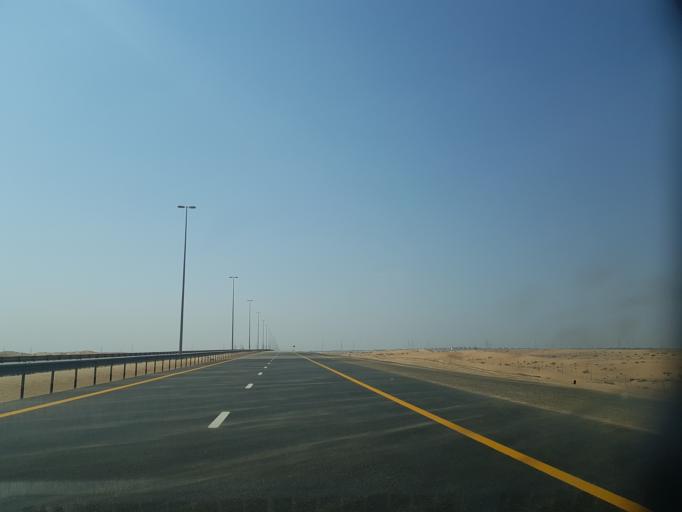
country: AE
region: Ash Shariqah
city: Sharjah
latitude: 25.2774
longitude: 55.6141
